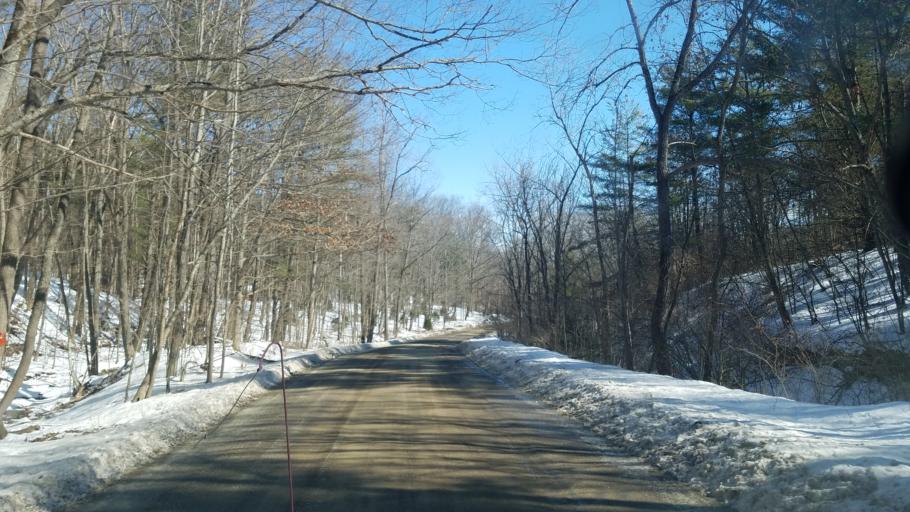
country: US
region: New York
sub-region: Allegany County
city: Alfred
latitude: 42.2474
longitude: -77.7161
